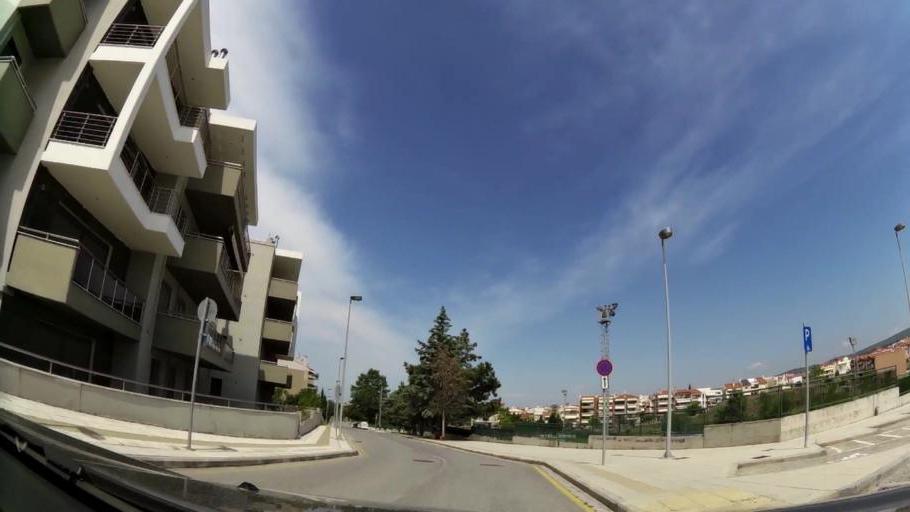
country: GR
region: Central Macedonia
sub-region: Nomos Thessalonikis
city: Pylaia
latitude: 40.6037
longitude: 22.9913
